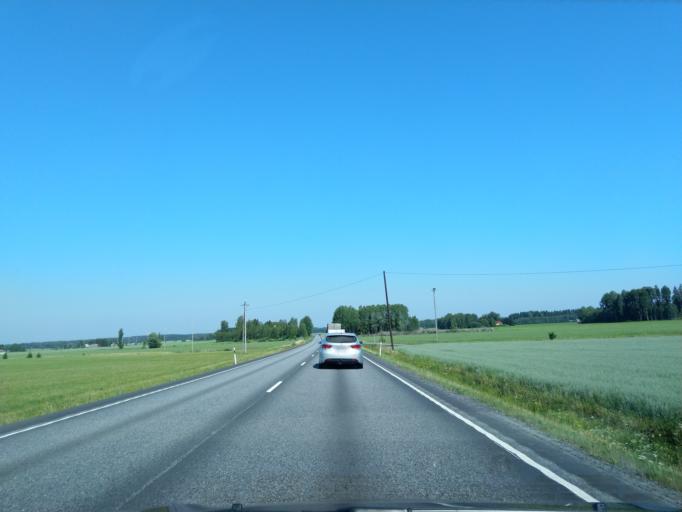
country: FI
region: Varsinais-Suomi
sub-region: Loimaa
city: Alastaro
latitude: 61.0839
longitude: 22.8968
